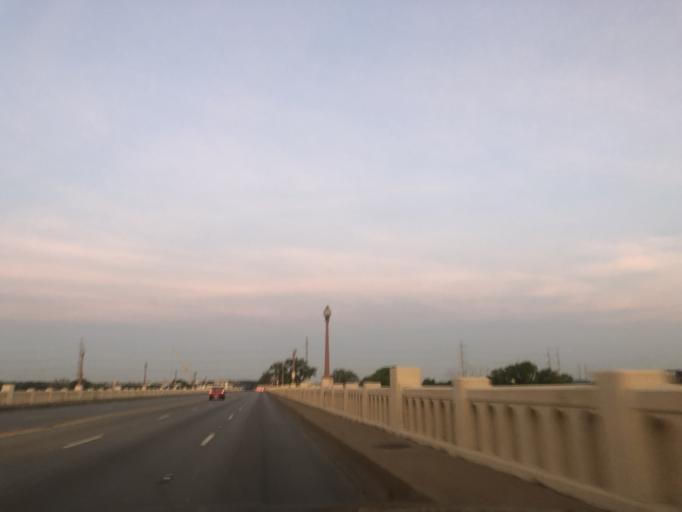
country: US
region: Texas
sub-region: Dallas County
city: Dallas
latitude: 32.7762
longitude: -96.8169
